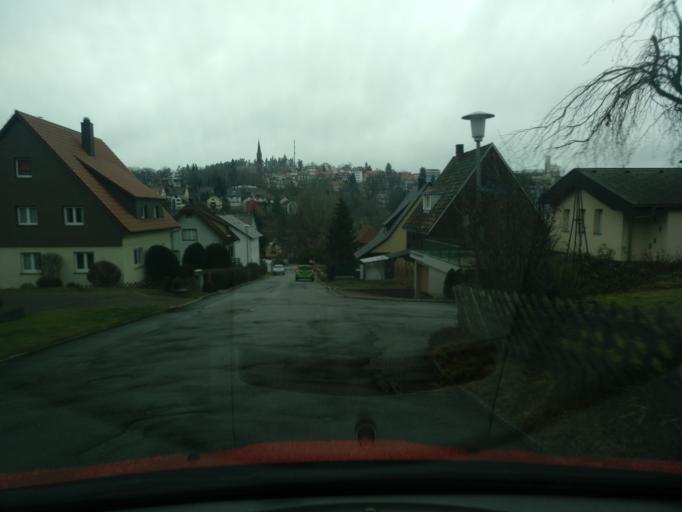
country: DE
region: Baden-Wuerttemberg
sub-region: Freiburg Region
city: Sankt Georgen im Schwarzwald
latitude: 48.1192
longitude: 8.3327
